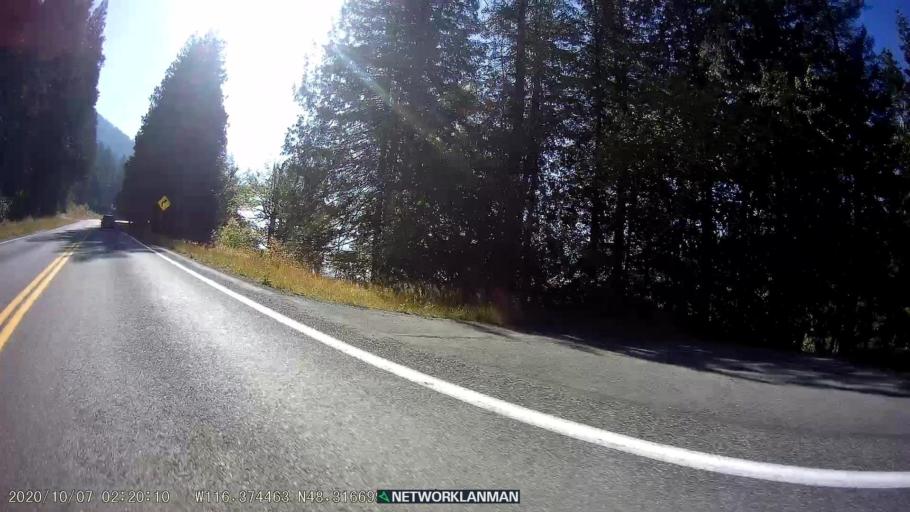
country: US
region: Idaho
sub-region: Bonner County
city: Ponderay
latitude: 48.3164
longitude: -116.3742
